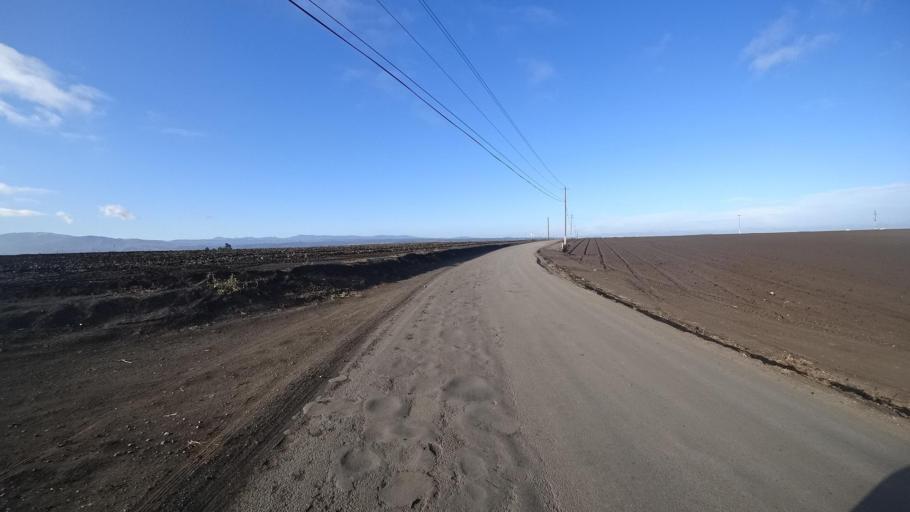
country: US
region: California
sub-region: Monterey County
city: Boronda
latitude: 36.7067
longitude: -121.7000
